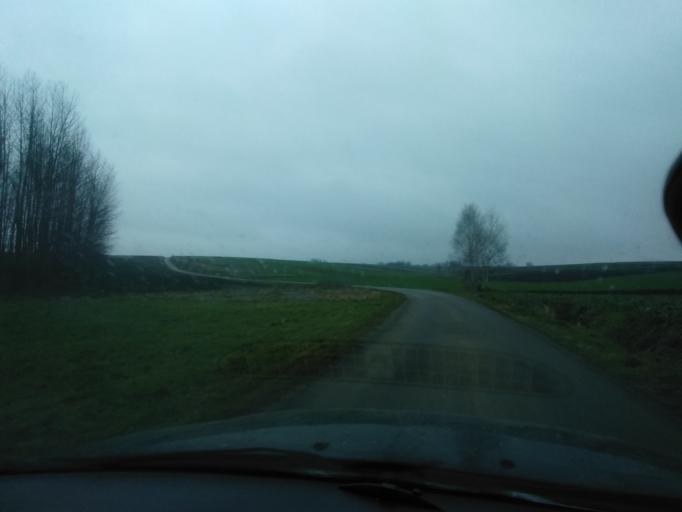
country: PL
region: Subcarpathian Voivodeship
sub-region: Powiat jaroslawski
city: Rokietnica
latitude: 49.9254
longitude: 22.6163
